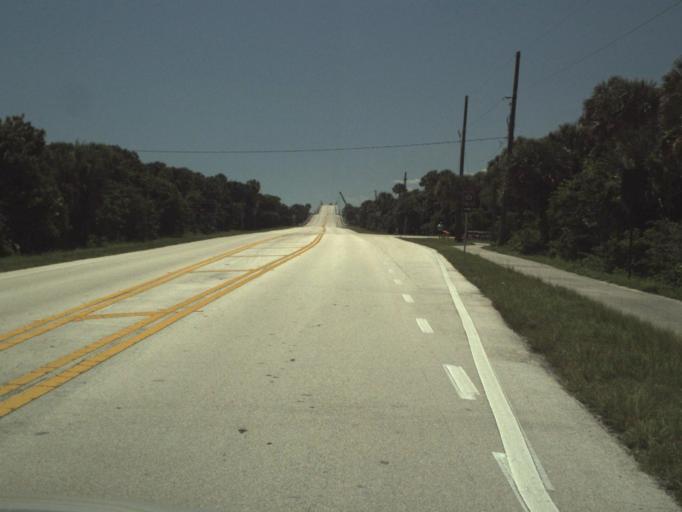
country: US
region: Florida
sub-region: Brevard County
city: Micco
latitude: 27.8659
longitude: -80.4514
